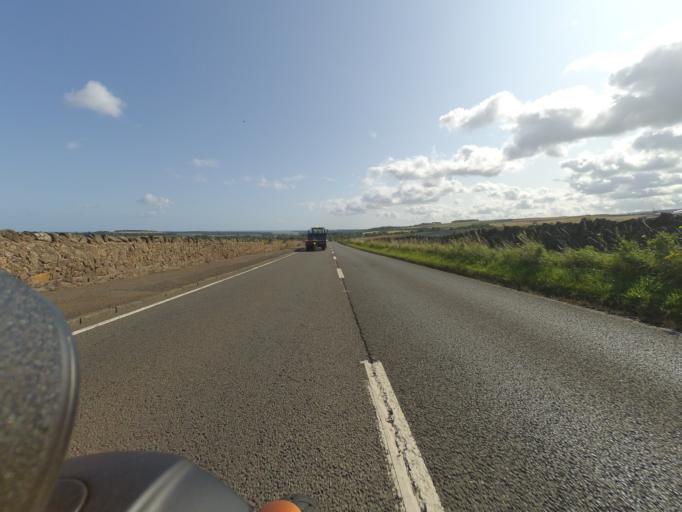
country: GB
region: Scotland
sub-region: East Lothian
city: East Linton
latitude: 55.9816
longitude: -2.6751
